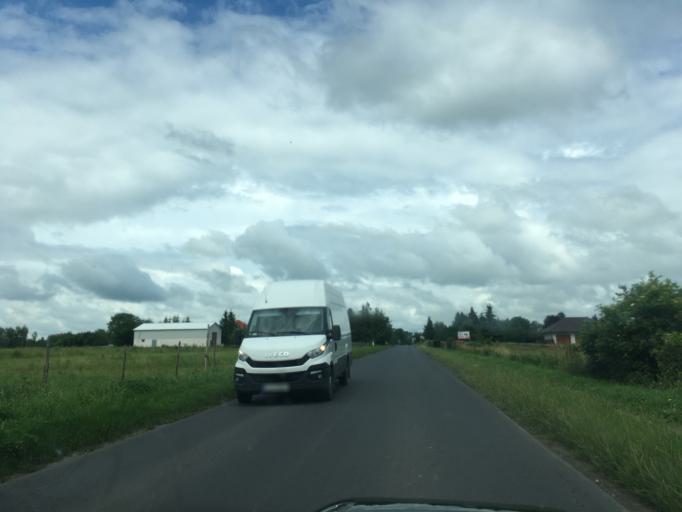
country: PL
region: Lublin Voivodeship
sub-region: Powiat swidnicki
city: Melgiew
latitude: 51.2120
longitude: 22.7467
